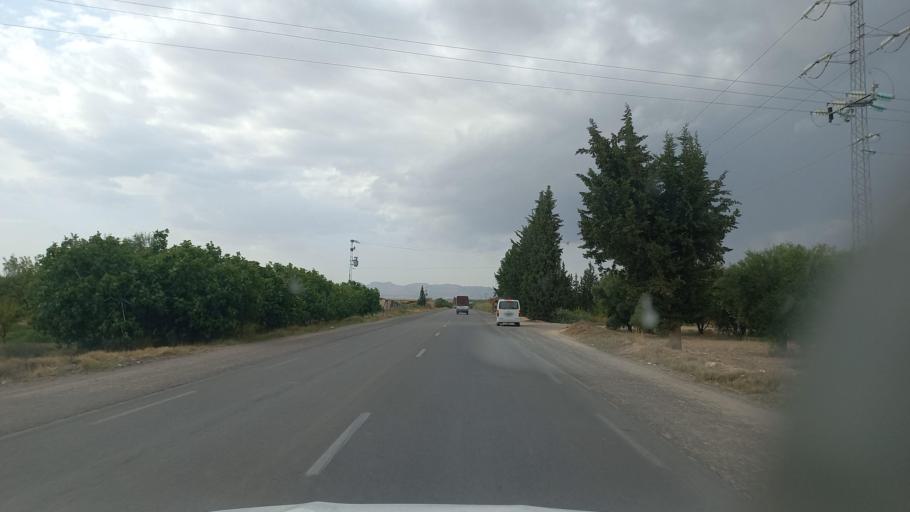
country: TN
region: Al Qasrayn
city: Sbiba
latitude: 35.3005
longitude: 9.0885
